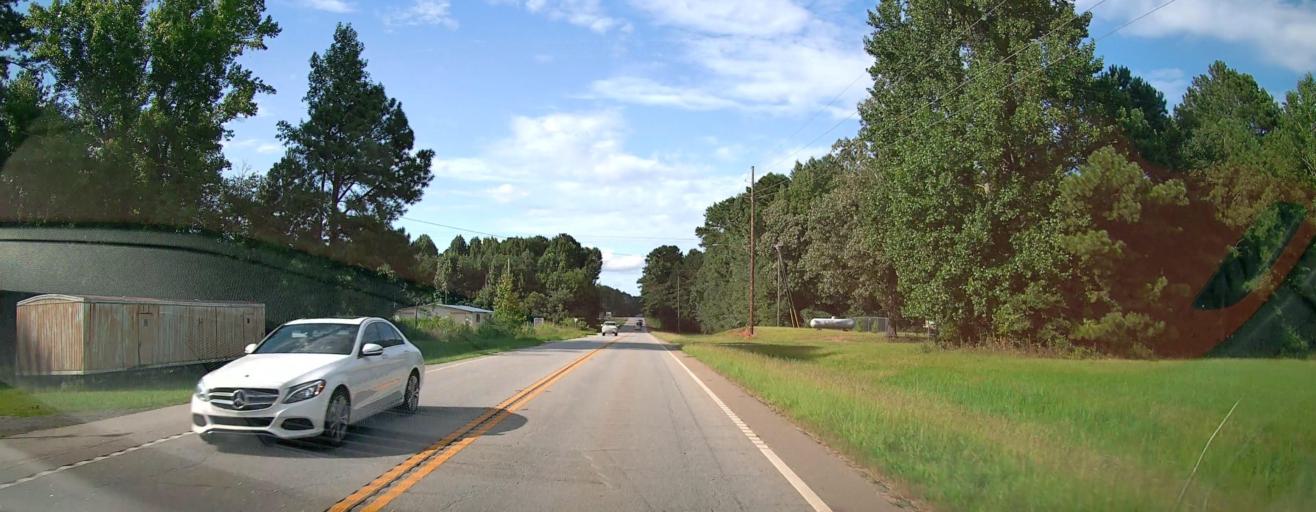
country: US
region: Georgia
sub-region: Coweta County
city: Senoia
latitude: 33.2335
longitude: -84.5666
